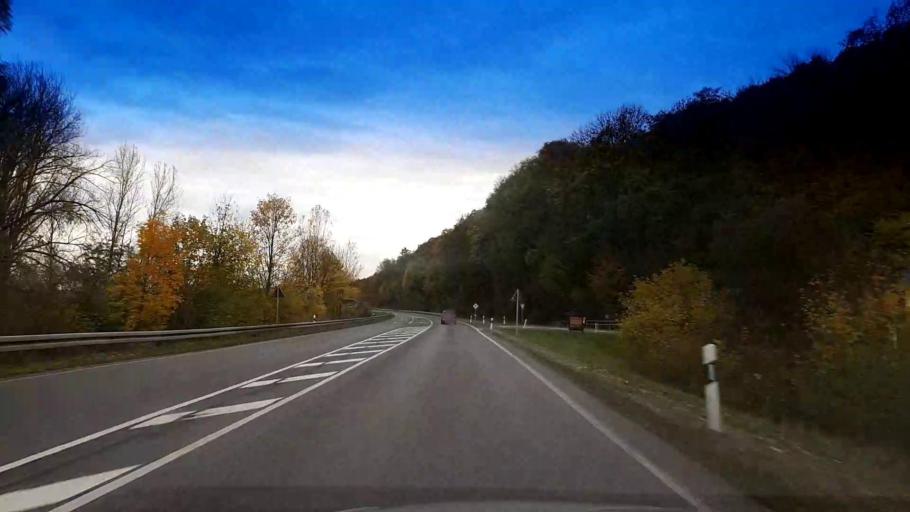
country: DE
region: Bavaria
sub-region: Regierungsbezirk Unterfranken
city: Stettfeld
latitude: 49.9446
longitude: 10.7267
